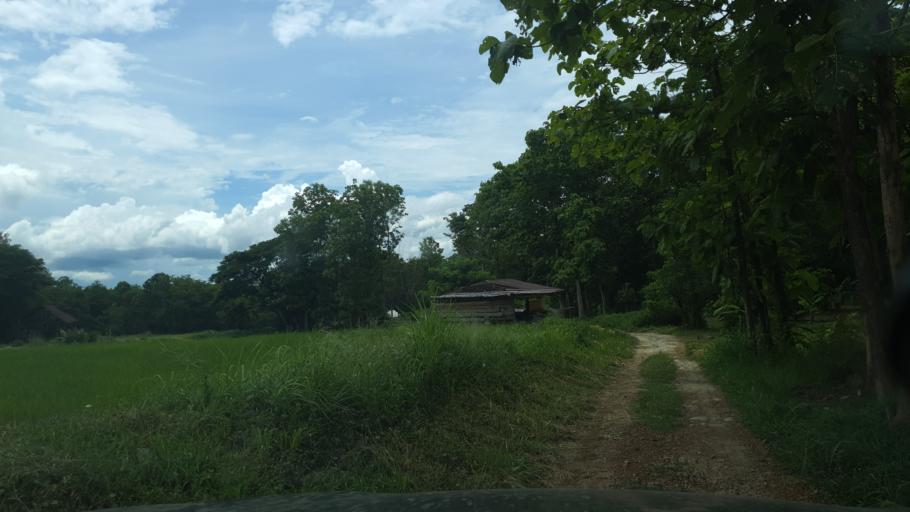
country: TH
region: Lampang
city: Sop Prap
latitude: 17.8549
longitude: 99.3971
